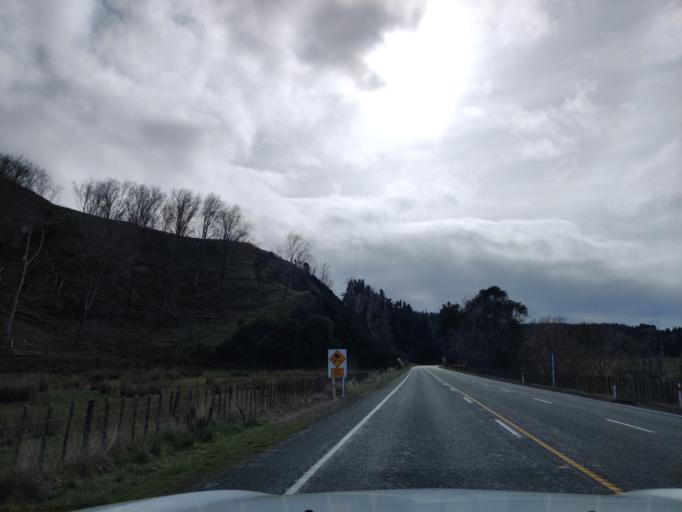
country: NZ
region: Manawatu-Wanganui
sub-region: Ruapehu District
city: Waiouru
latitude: -39.7647
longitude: 175.8020
